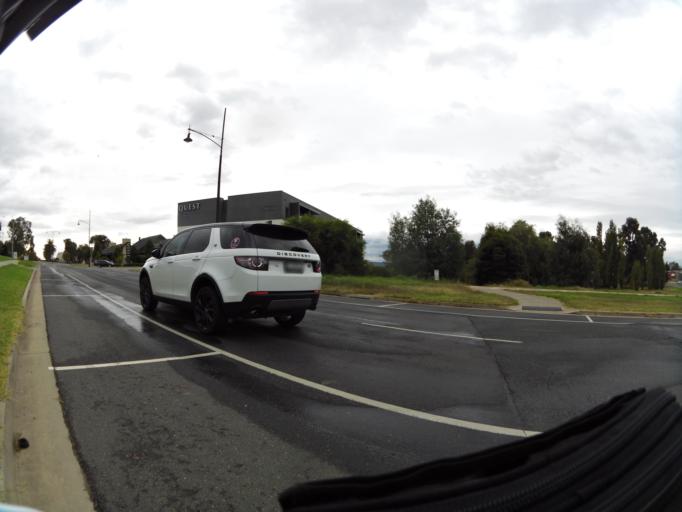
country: AU
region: Victoria
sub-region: Wodonga
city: Wodonga
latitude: -36.1229
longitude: 146.8931
